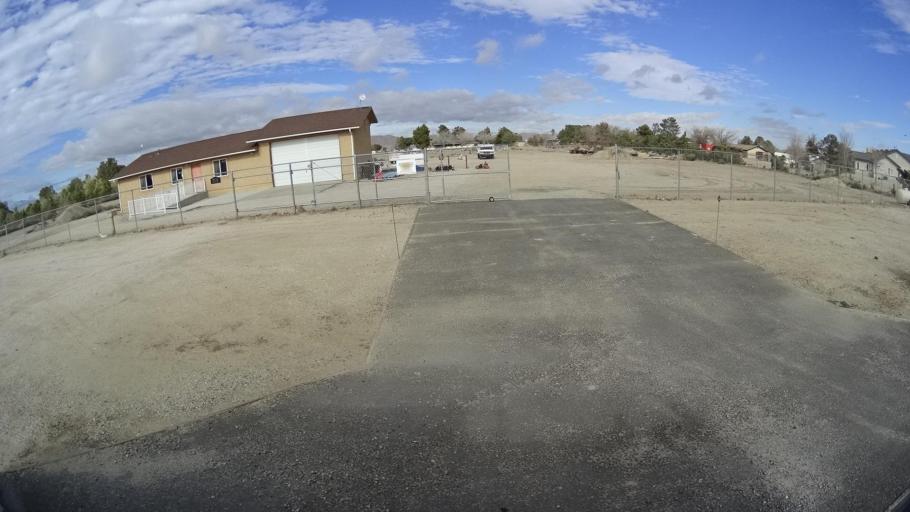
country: US
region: California
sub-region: Kern County
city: Rosamond
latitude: 34.8202
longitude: -118.2611
